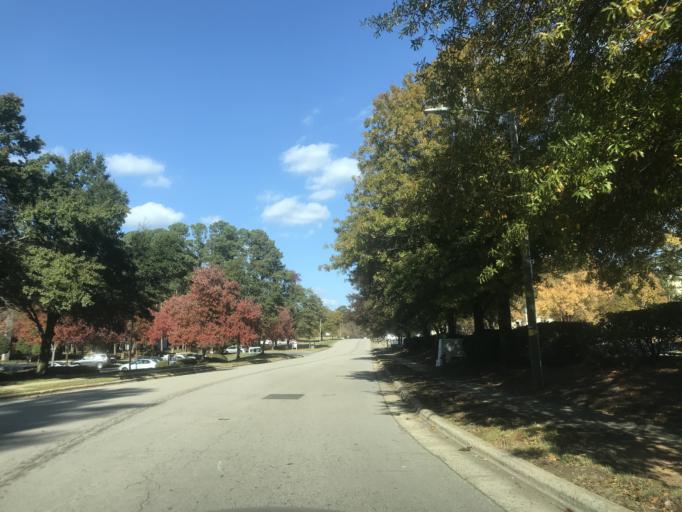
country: US
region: North Carolina
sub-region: Wake County
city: Raleigh
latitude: 35.8287
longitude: -78.6222
